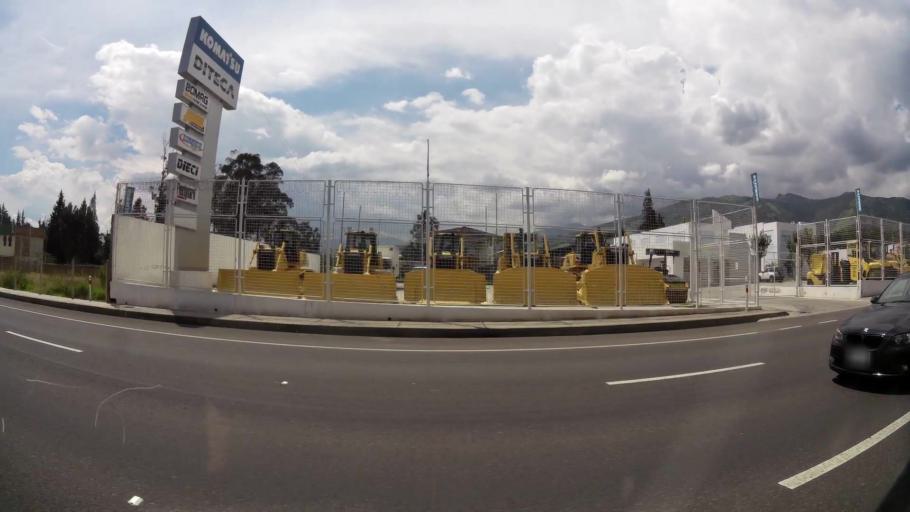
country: EC
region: Pichincha
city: Sangolqui
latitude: -0.2008
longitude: -78.3361
